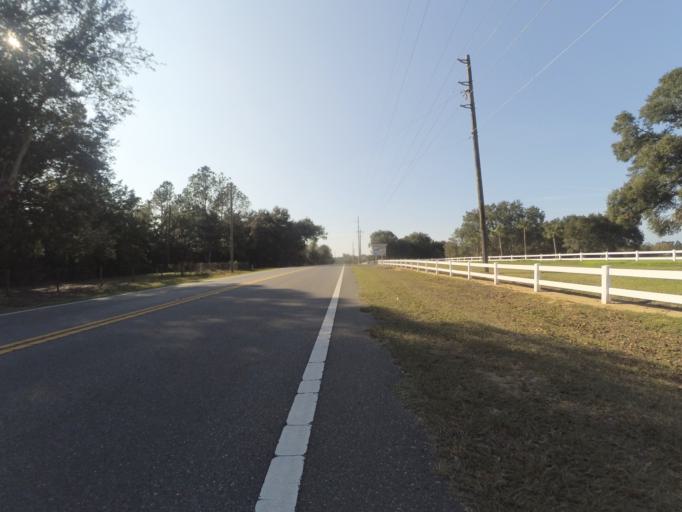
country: US
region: Florida
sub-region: Lake County
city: Umatilla
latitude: 28.9895
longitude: -81.7182
